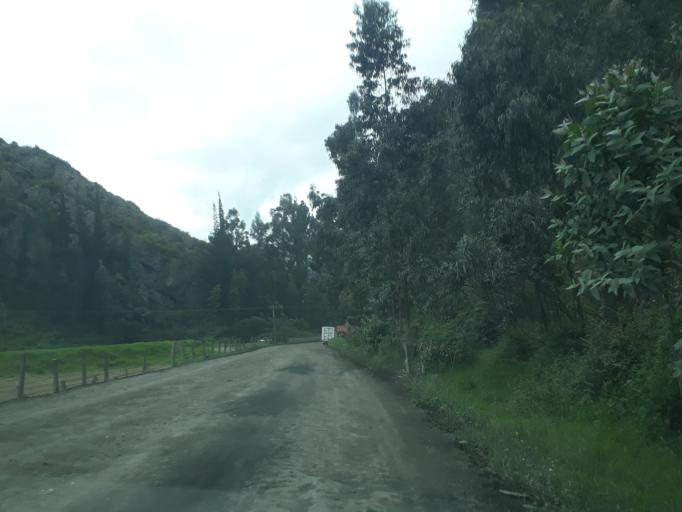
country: CO
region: Cundinamarca
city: Lenguazaque
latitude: 5.3285
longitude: -73.7014
